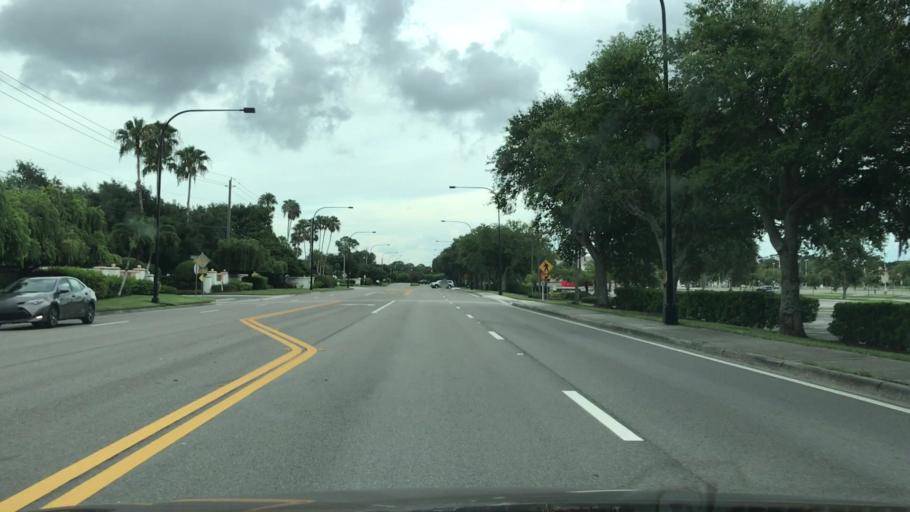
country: US
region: Florida
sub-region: Sarasota County
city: Vamo
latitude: 27.2367
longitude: -82.4930
